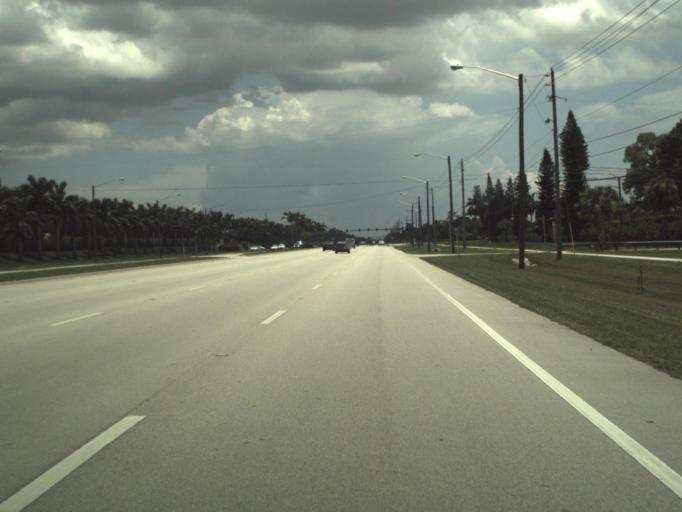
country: US
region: Florida
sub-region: Palm Beach County
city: Royal Palm Beach
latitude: 26.7090
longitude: -80.1938
